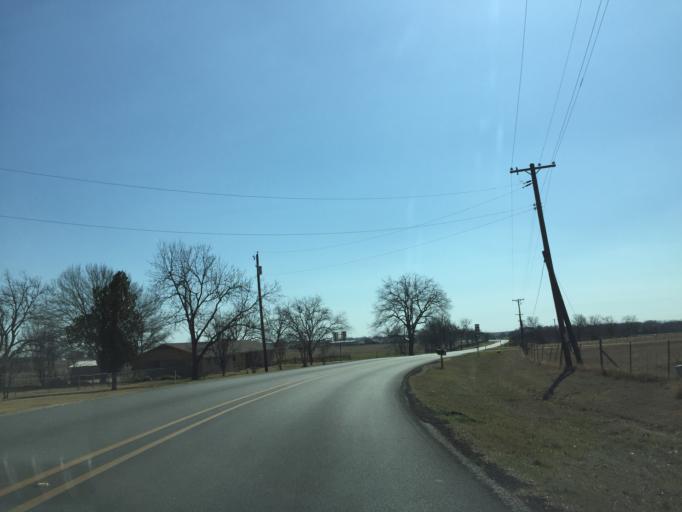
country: US
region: Texas
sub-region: Williamson County
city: Serenada
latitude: 30.7369
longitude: -97.5970
